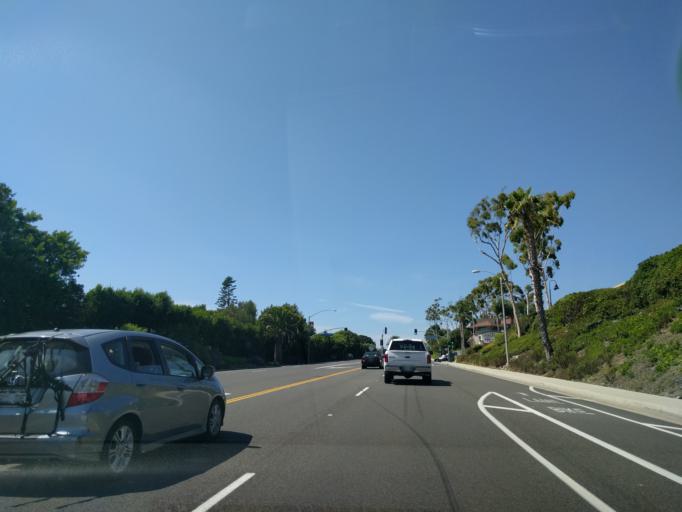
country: US
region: California
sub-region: Orange County
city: Dana Point
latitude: 33.4845
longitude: -117.7243
